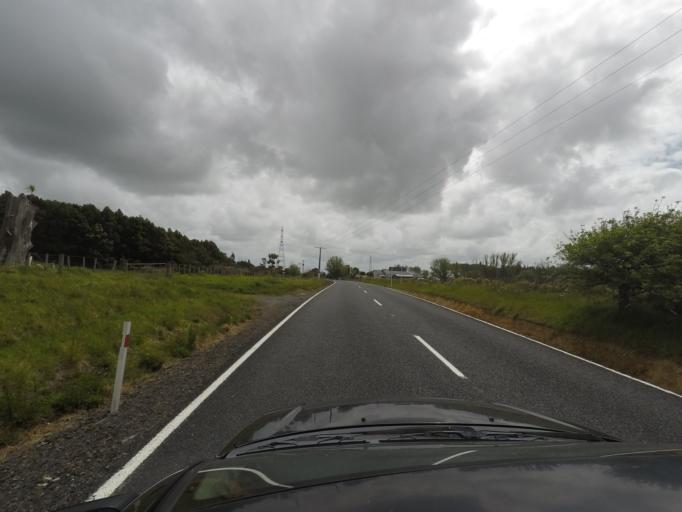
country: NZ
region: Auckland
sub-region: Auckland
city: Parakai
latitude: -36.5071
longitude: 174.4626
